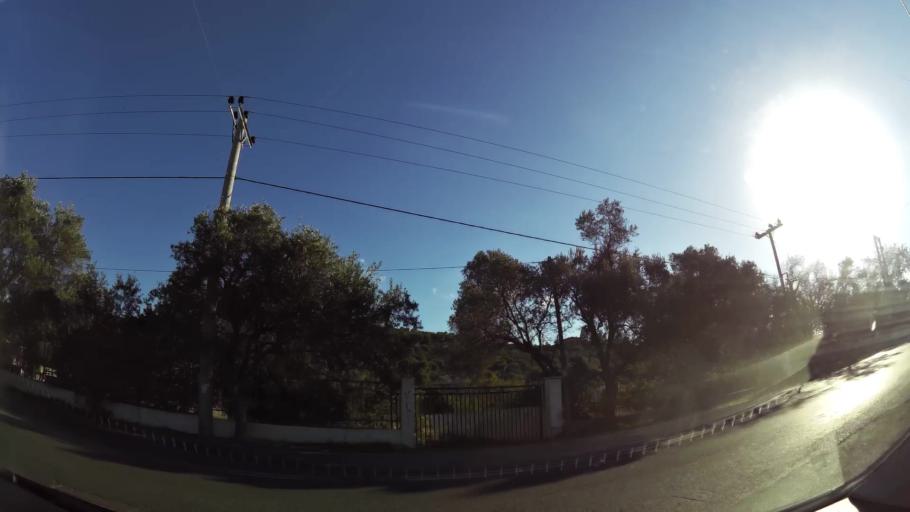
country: GR
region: Attica
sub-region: Nomarchia Anatolikis Attikis
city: Rafina
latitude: 38.0186
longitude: 23.9850
